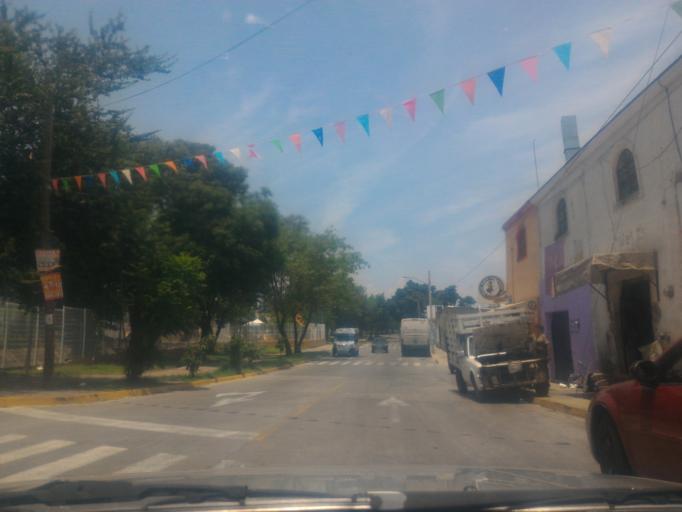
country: MX
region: Jalisco
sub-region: Tlajomulco de Zuniga
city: Altus Bosques
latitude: 20.6202
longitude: -103.3660
